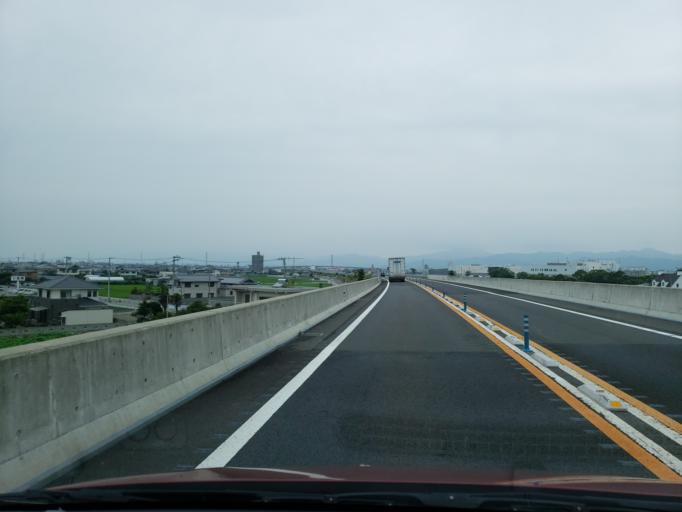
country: JP
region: Tokushima
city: Tokushima-shi
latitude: 34.1144
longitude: 134.5890
